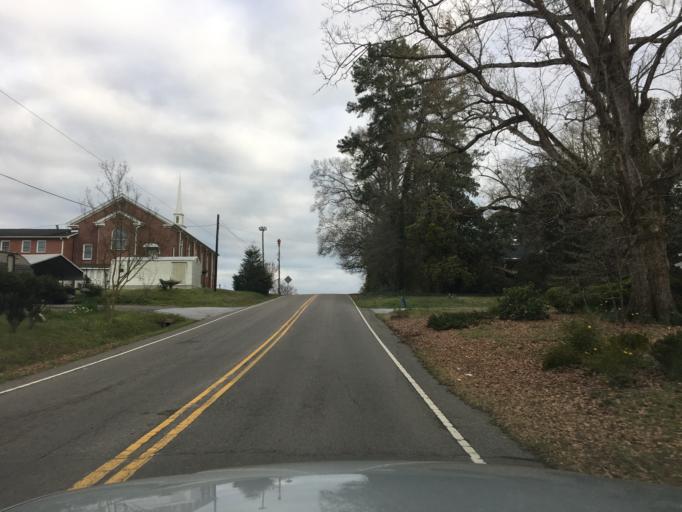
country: US
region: South Carolina
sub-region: Saluda County
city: Saluda
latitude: 34.0036
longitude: -81.7737
